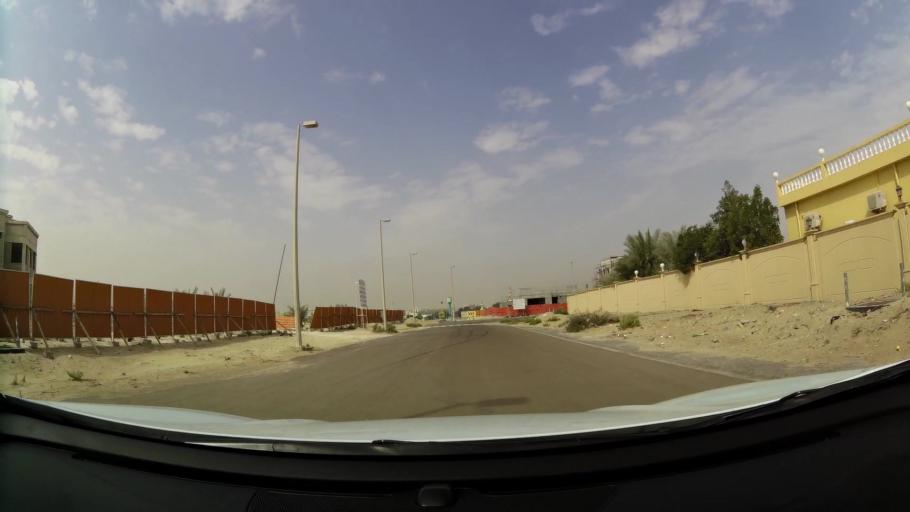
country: AE
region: Abu Dhabi
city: Abu Dhabi
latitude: 24.2741
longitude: 54.6642
